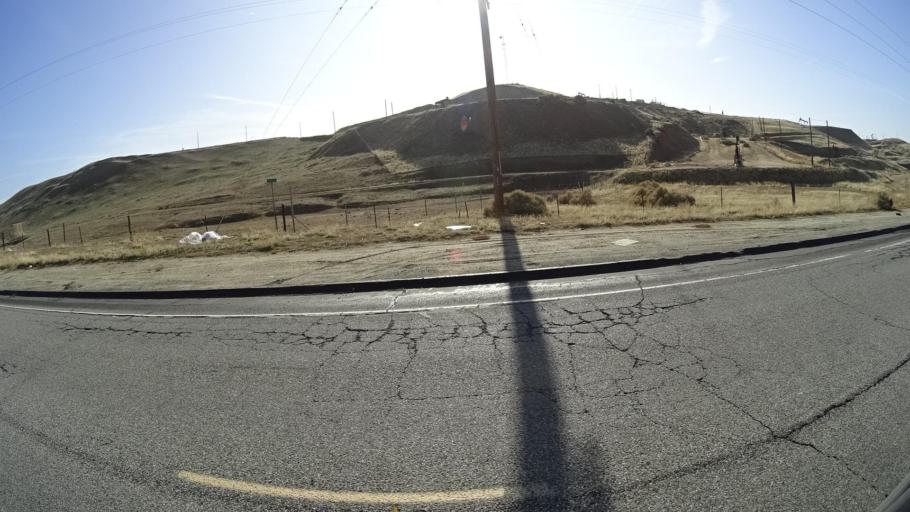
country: US
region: California
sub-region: Kern County
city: Oildale
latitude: 35.4889
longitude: -119.0033
